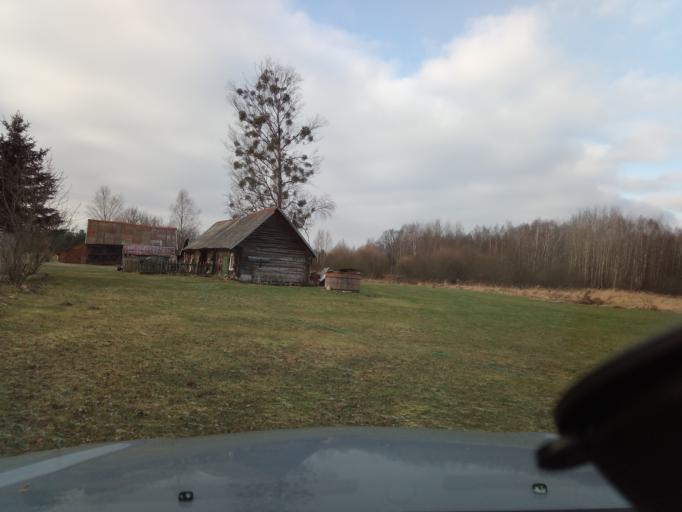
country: LT
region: Alytaus apskritis
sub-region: Alytaus rajonas
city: Daugai
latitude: 54.1162
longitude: 24.2305
